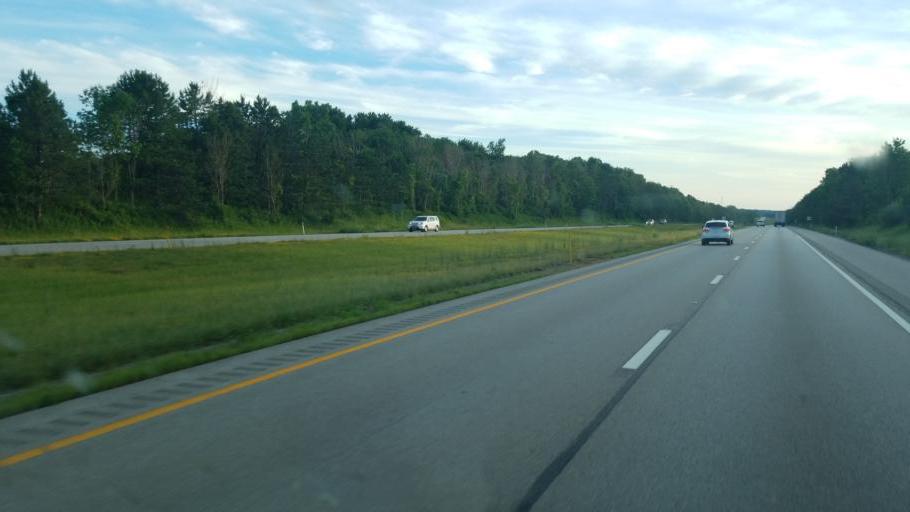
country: US
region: Ohio
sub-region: Ashtabula County
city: North Kingsville
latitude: 41.8988
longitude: -80.6251
